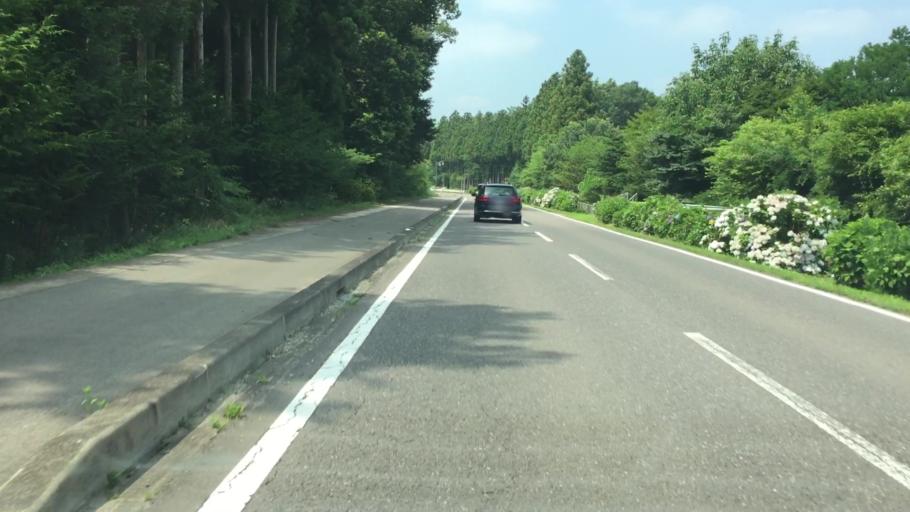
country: JP
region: Tochigi
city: Kuroiso
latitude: 36.9891
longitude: 139.9900
